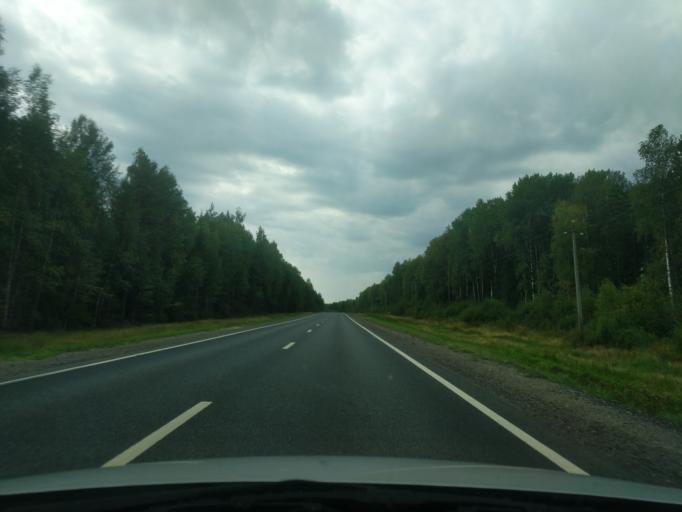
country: RU
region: Kostroma
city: Manturovo
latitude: 58.1584
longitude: 44.3892
